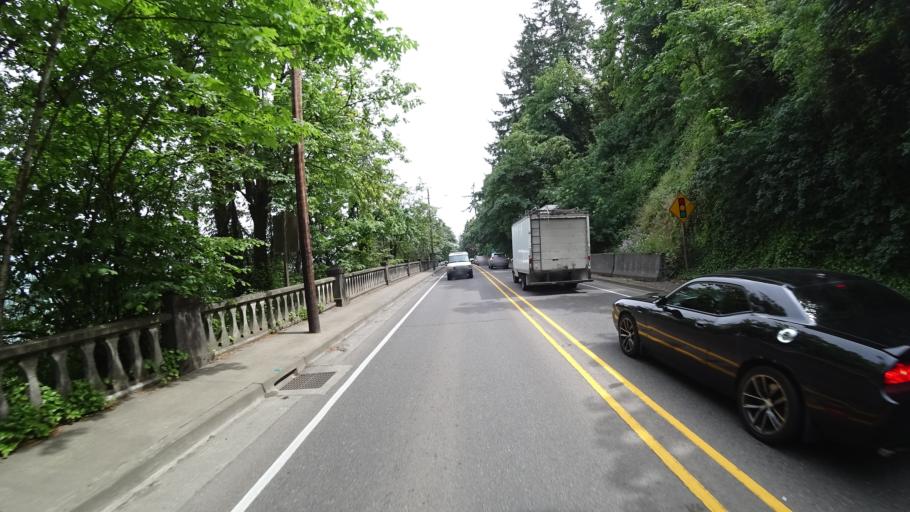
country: US
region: Oregon
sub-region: Washington County
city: West Haven
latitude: 45.5839
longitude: -122.7697
